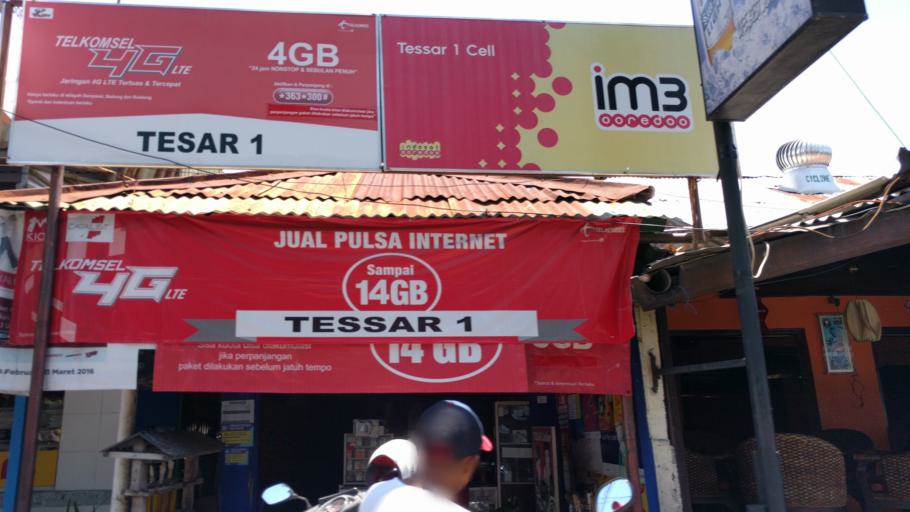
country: ID
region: Bali
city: Banjar Medura
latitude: -8.7048
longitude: 115.2589
